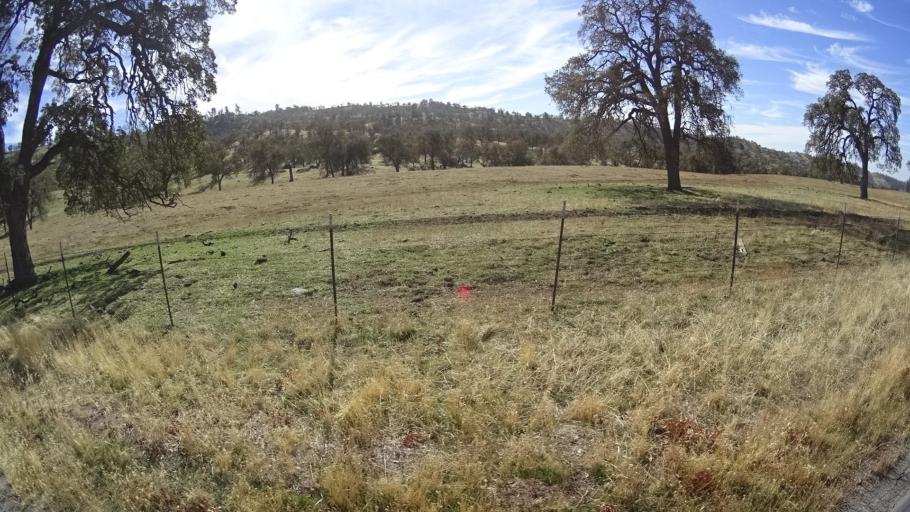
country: US
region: California
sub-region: Kern County
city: Alta Sierra
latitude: 35.6298
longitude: -118.7850
